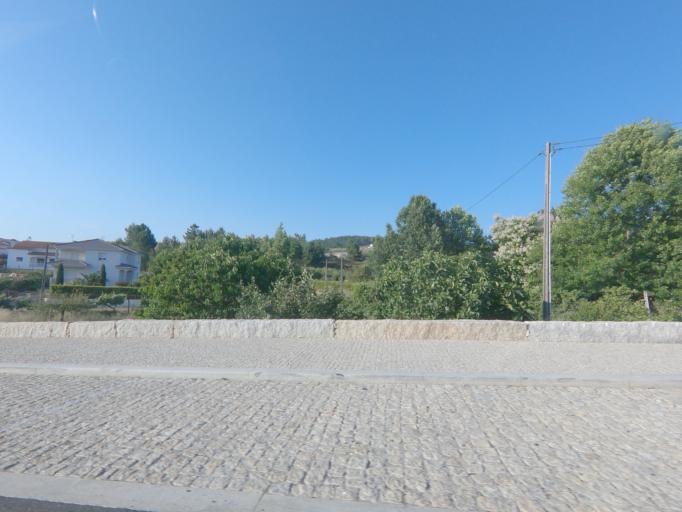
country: PT
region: Vila Real
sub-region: Sabrosa
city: Vilela
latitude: 41.2667
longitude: -7.6268
